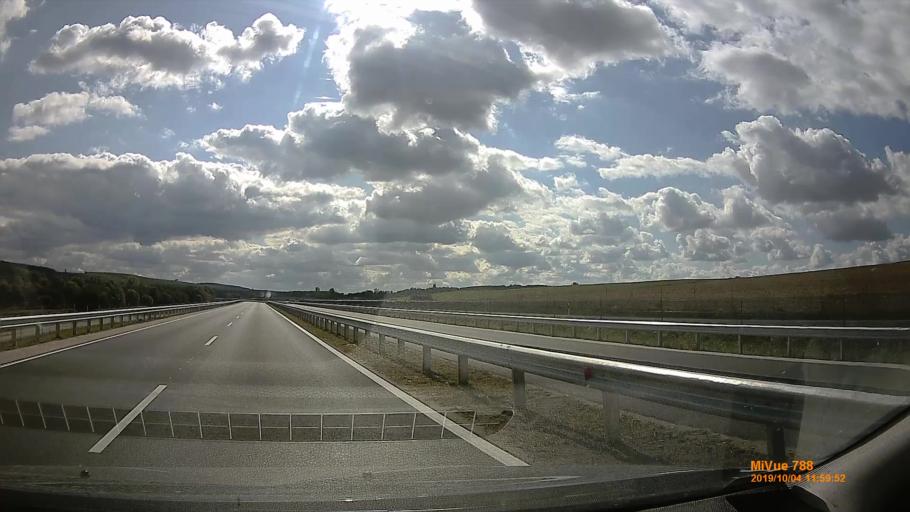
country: HU
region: Somogy
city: Karad
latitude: 46.6323
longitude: 17.7913
